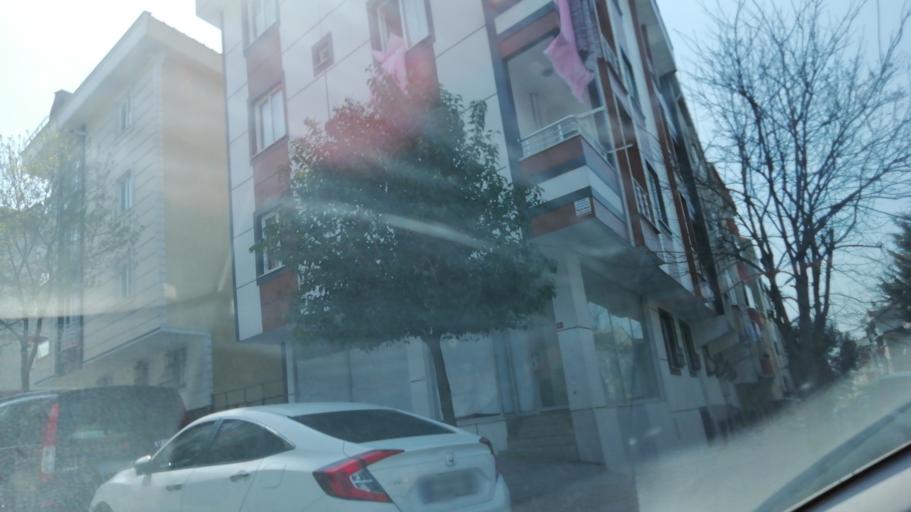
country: TR
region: Istanbul
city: Mahmutbey
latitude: 41.0382
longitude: 28.8222
